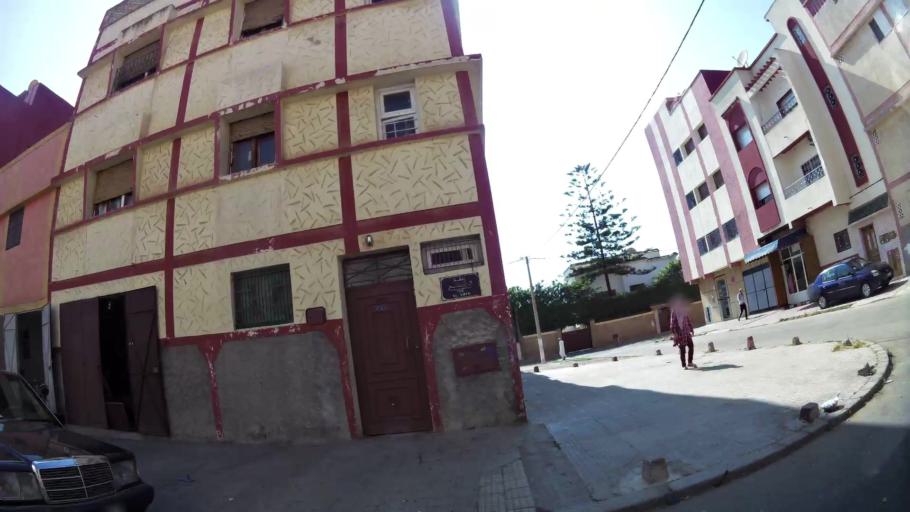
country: MA
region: Rabat-Sale-Zemmour-Zaer
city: Sale
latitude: 34.0460
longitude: -6.7832
